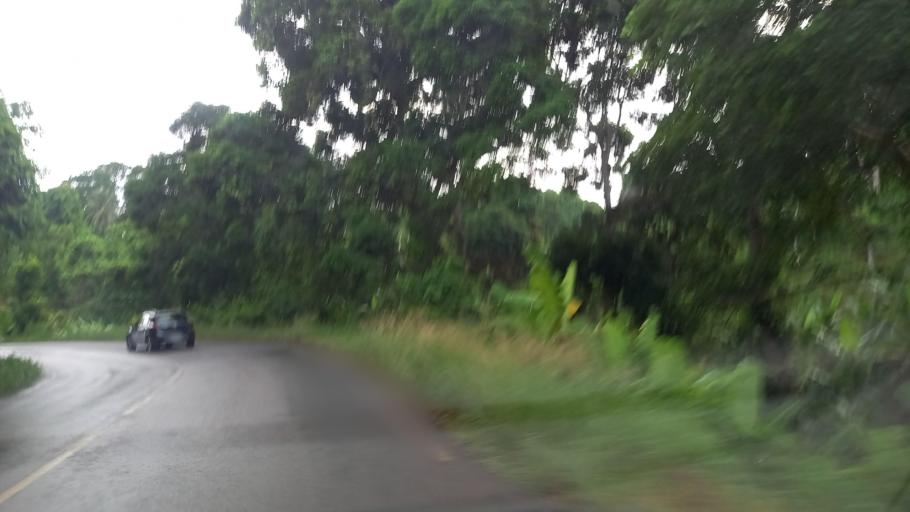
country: YT
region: Dembeni
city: Dembeni
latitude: -12.8404
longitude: 45.1669
